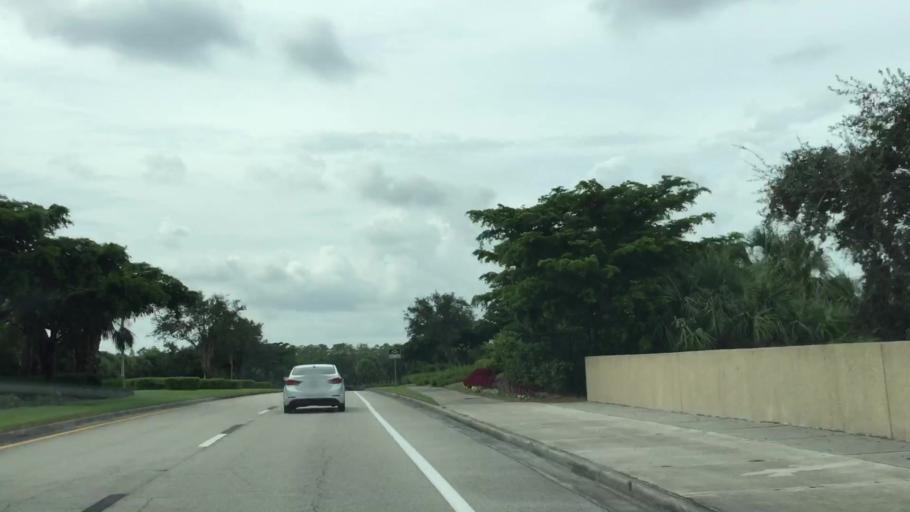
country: US
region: Florida
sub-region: Lee County
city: Estero
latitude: 26.4132
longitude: -81.7856
